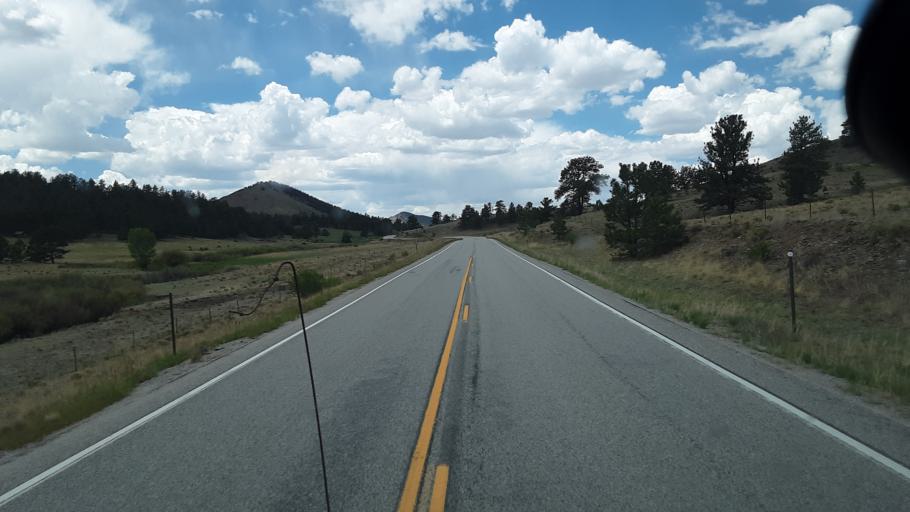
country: US
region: Colorado
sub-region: Teller County
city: Cripple Creek
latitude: 38.7928
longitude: -105.5912
